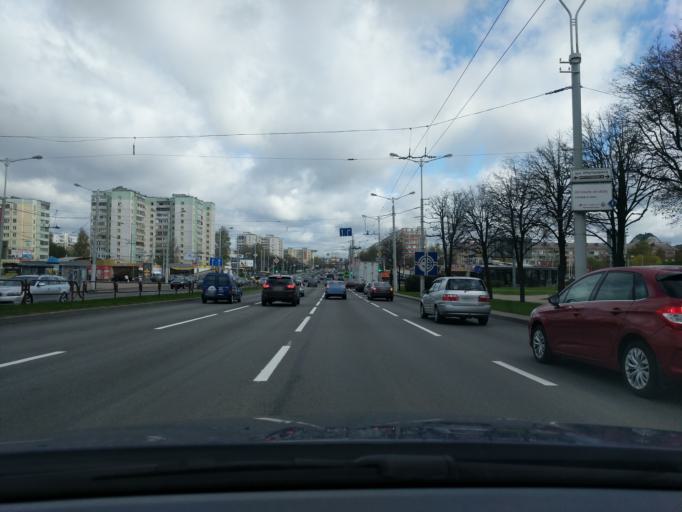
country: BY
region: Minsk
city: Novoye Medvezhino
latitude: 53.9082
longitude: 27.4959
